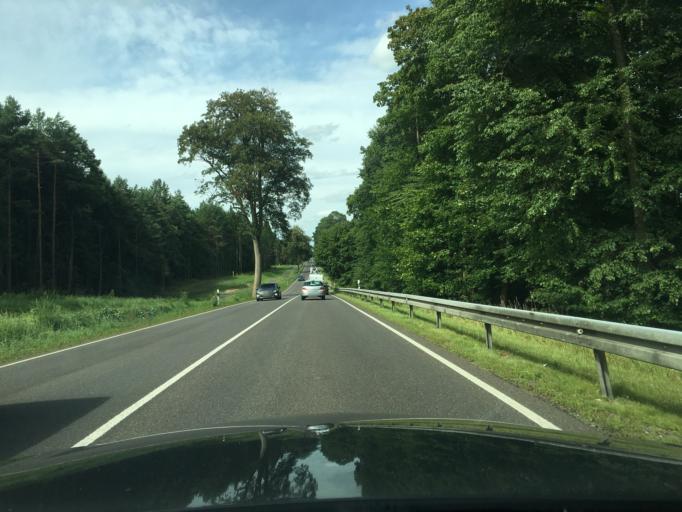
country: DE
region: Mecklenburg-Vorpommern
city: Neustrelitz
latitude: 53.2771
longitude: 13.1126
